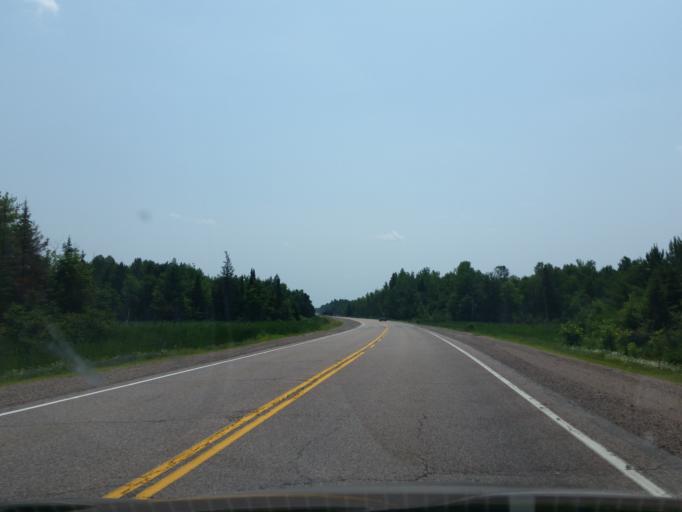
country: CA
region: Ontario
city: Petawawa
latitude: 45.8712
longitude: -77.2981
